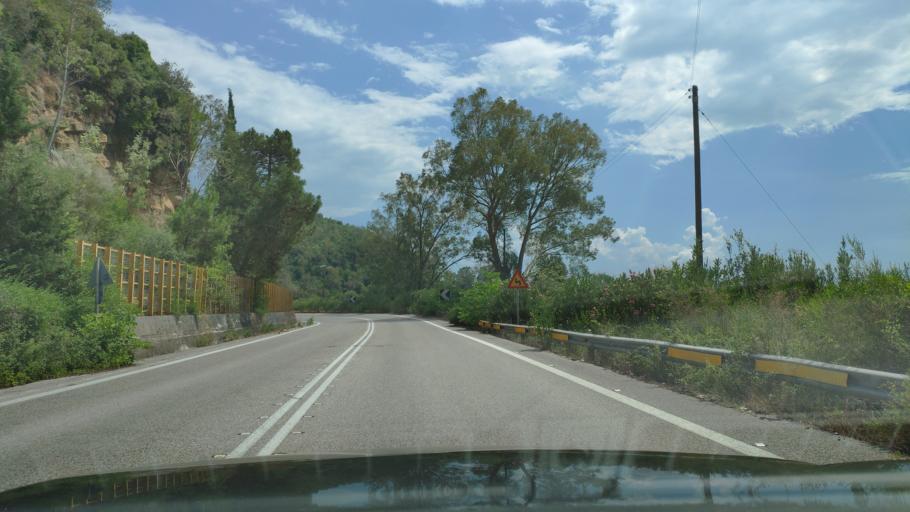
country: GR
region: West Greece
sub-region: Nomos Aitolias kai Akarnanias
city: Menidi
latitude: 39.0342
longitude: 21.1263
